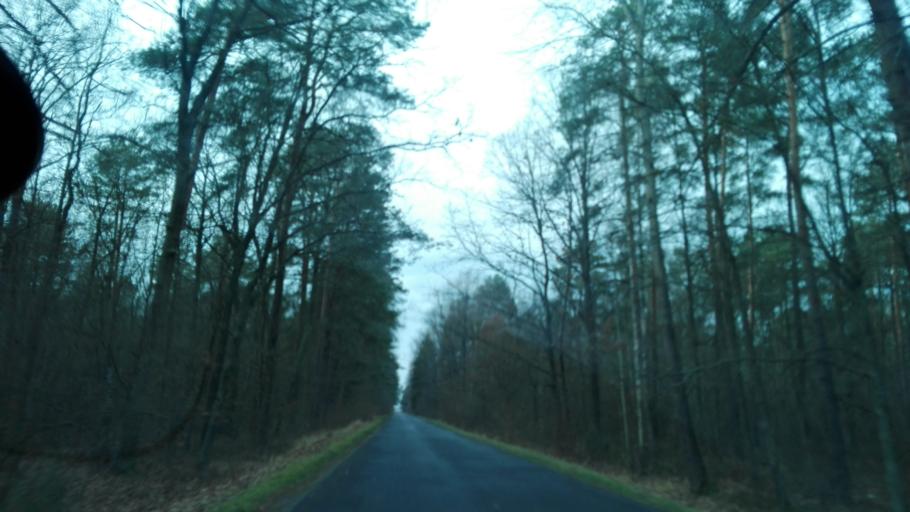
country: PL
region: Lublin Voivodeship
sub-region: Powiat bialski
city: Sosnowka
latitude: 51.7458
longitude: 23.3635
